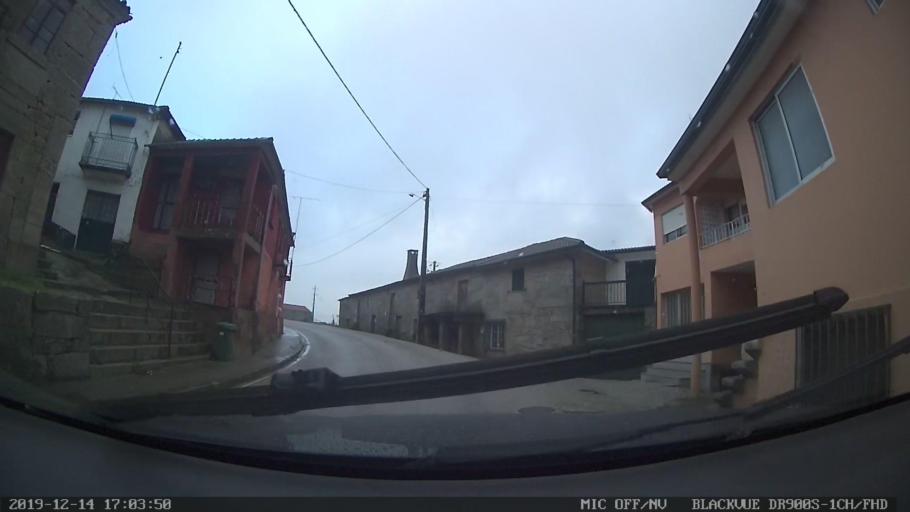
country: PT
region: Vila Real
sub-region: Vila Pouca de Aguiar
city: Vila Pouca de Aguiar
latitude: 41.4445
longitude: -7.5712
